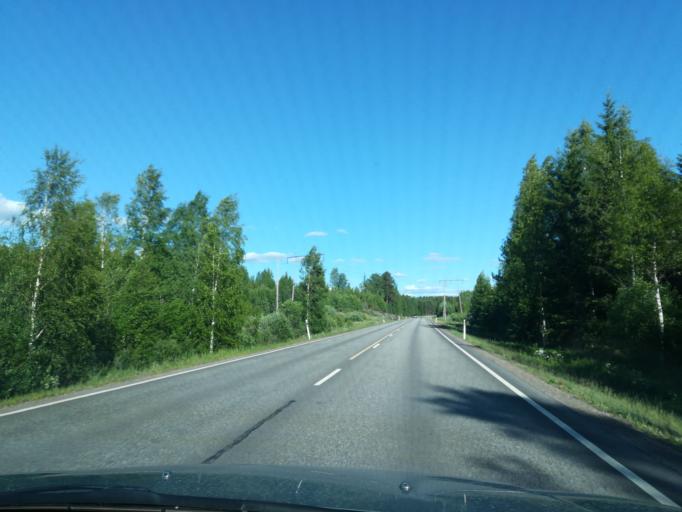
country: FI
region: South Karelia
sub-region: Imatra
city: Ruokolahti
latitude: 61.3505
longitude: 28.7498
